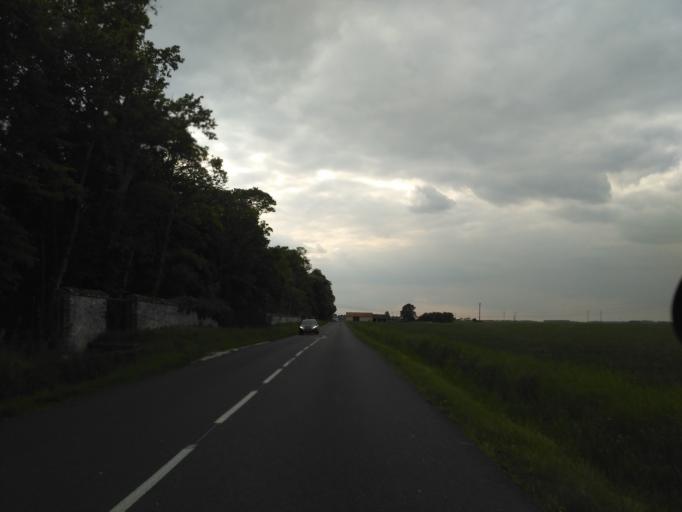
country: FR
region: Ile-de-France
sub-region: Departement de Seine-et-Marne
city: Rubelles
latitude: 48.5669
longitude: 2.6854
